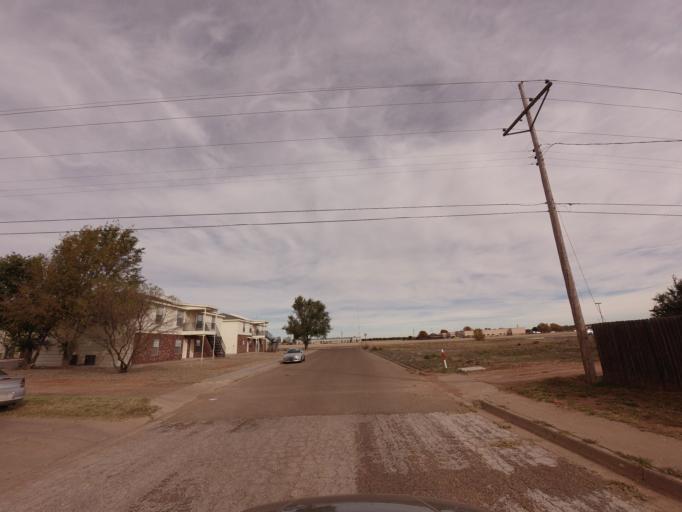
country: US
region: New Mexico
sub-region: Curry County
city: Clovis
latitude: 34.4303
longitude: -103.2095
